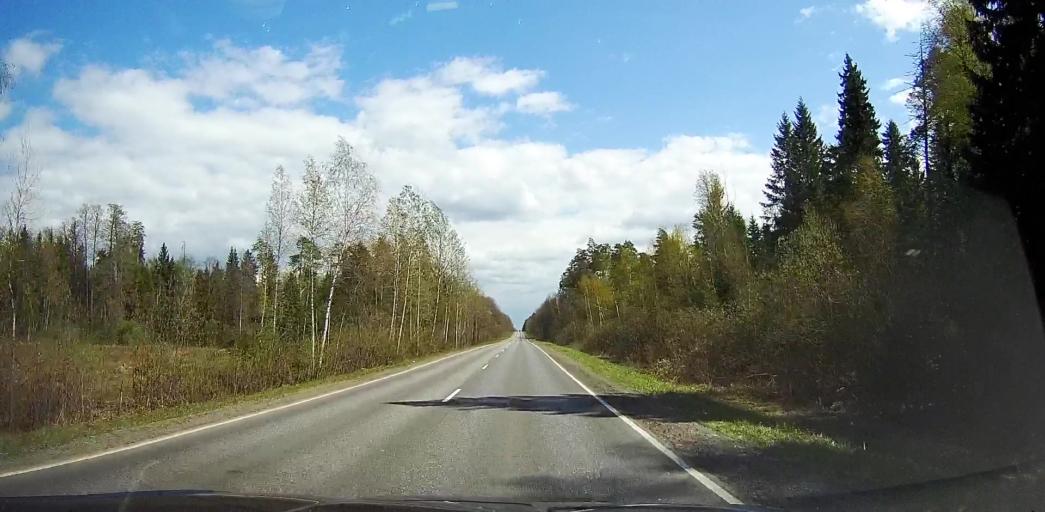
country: RU
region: Moskovskaya
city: Imeni Tsyurupy
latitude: 55.5513
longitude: 38.7388
